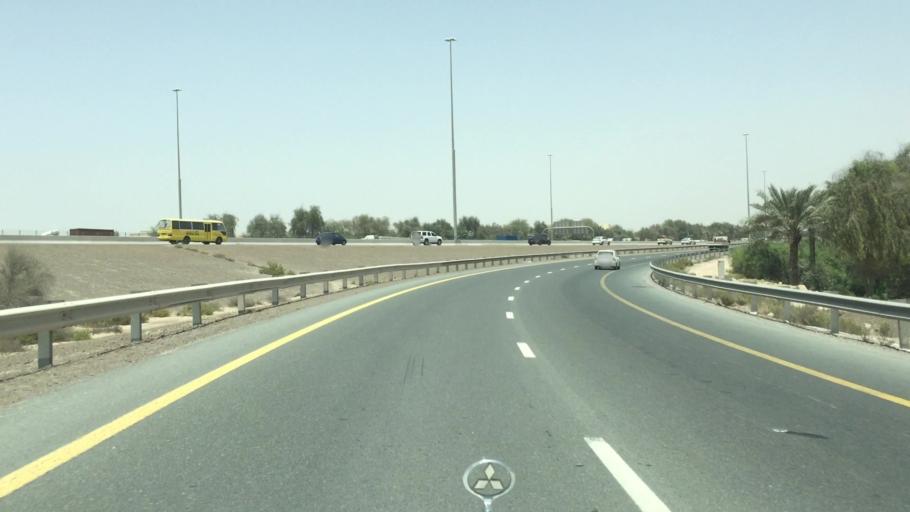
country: AE
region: Dubai
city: Dubai
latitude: 25.1207
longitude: 55.3675
